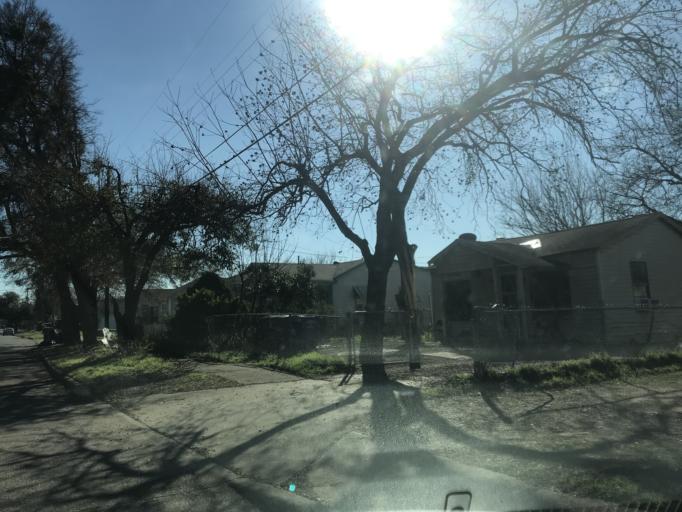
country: US
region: Texas
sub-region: Dallas County
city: Cockrell Hill
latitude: 32.7763
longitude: -96.9098
